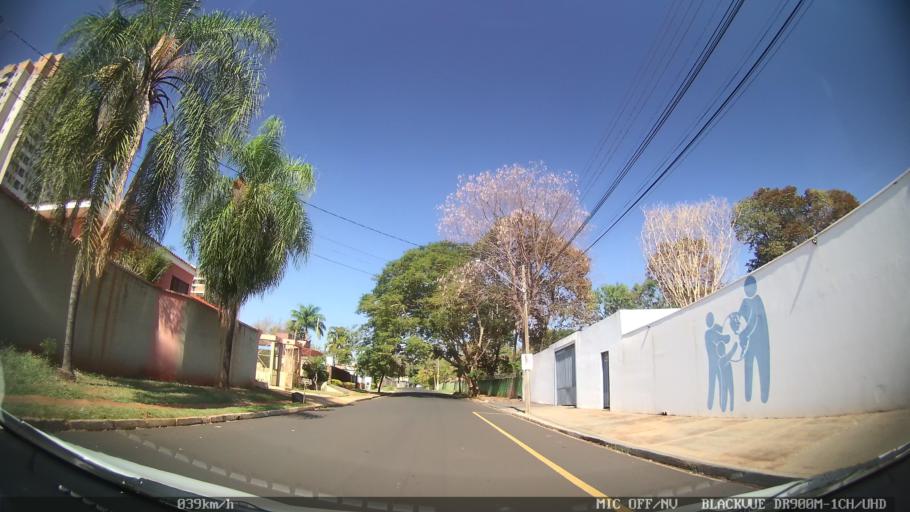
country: BR
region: Sao Paulo
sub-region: Ribeirao Preto
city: Ribeirao Preto
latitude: -21.2011
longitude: -47.7772
